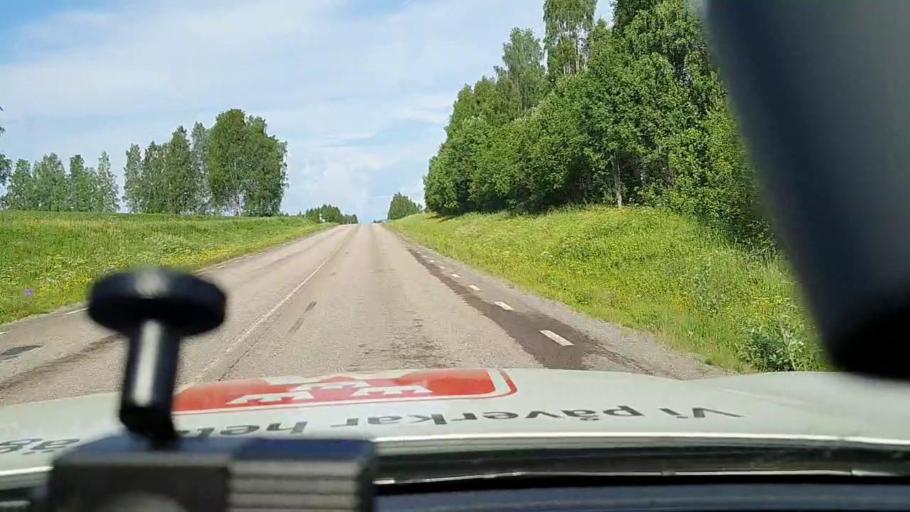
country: SE
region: Norrbotten
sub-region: Alvsbyns Kommun
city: AElvsbyn
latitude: 66.0142
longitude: 21.1656
